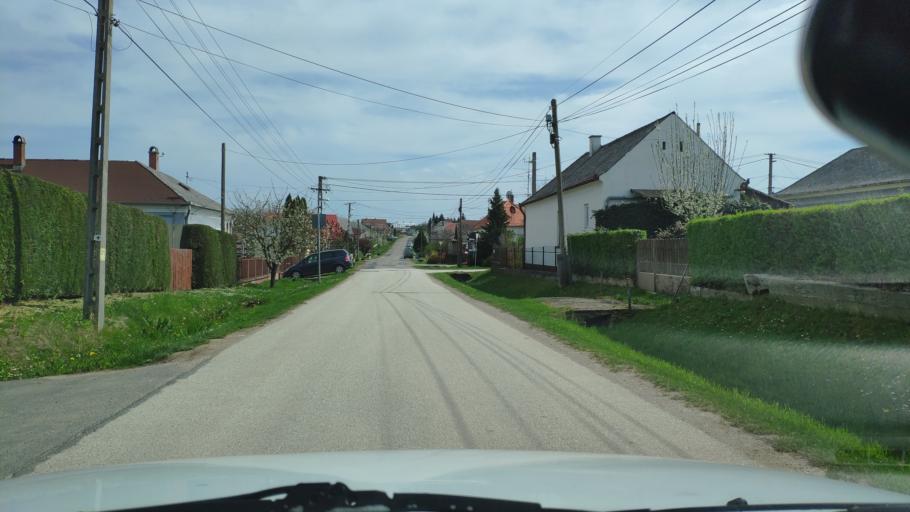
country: HU
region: Zala
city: Nagykanizsa
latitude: 46.4242
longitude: 17.0254
